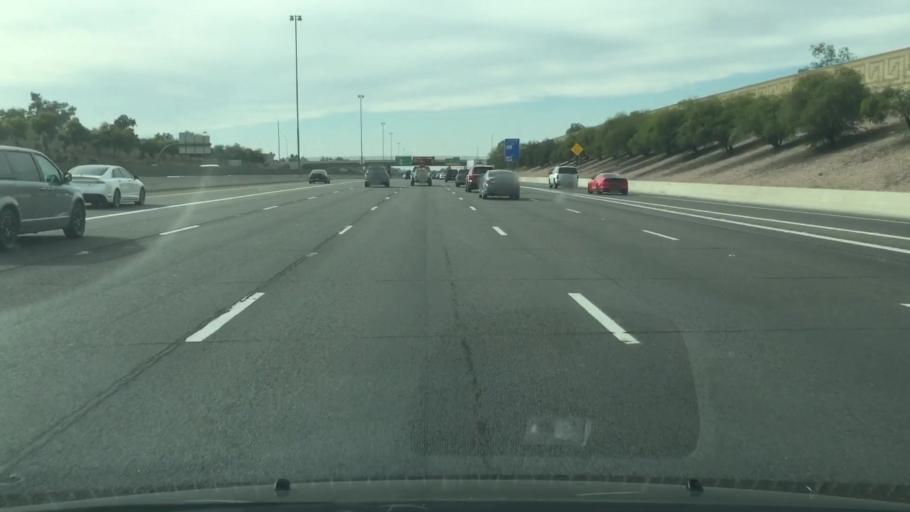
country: US
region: Arizona
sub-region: Maricopa County
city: San Carlos
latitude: 33.3864
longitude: -111.8447
